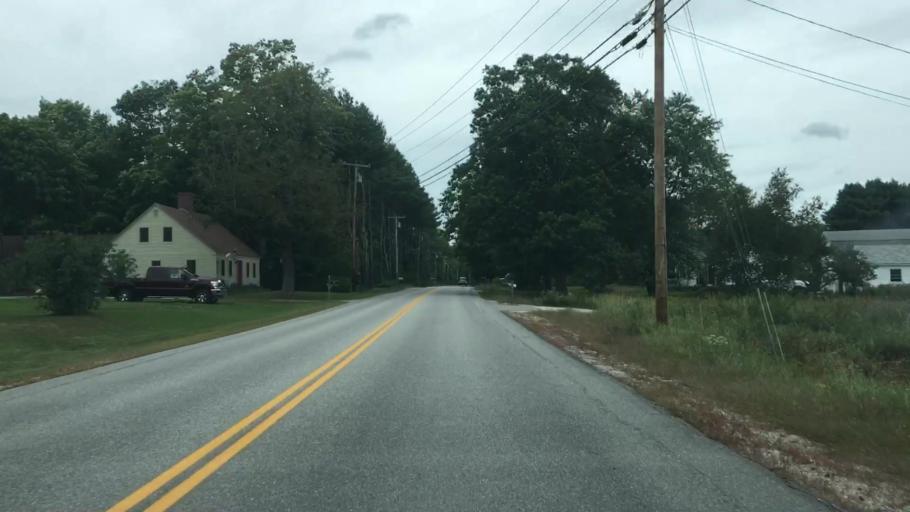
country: US
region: Maine
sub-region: Cumberland County
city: Yarmouth
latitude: 43.8295
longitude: -70.1972
